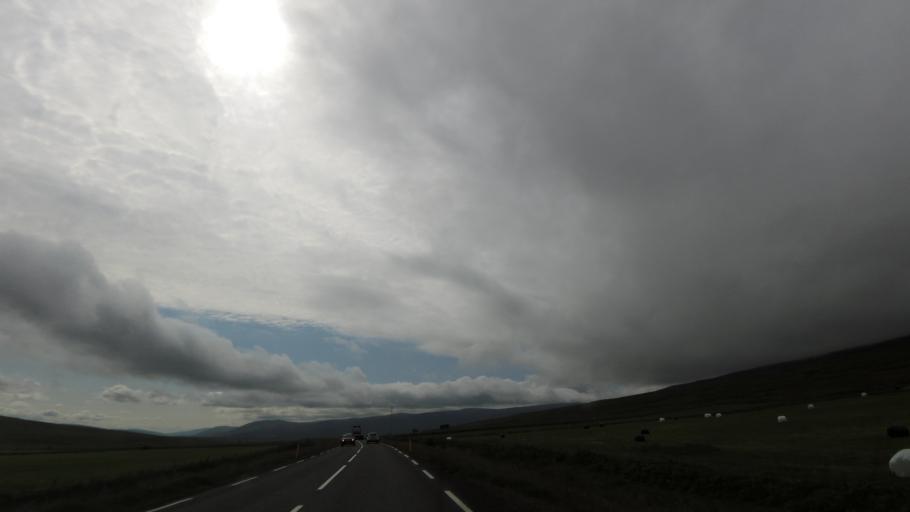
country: IS
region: Northeast
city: Laugar
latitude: 65.7445
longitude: -17.5914
